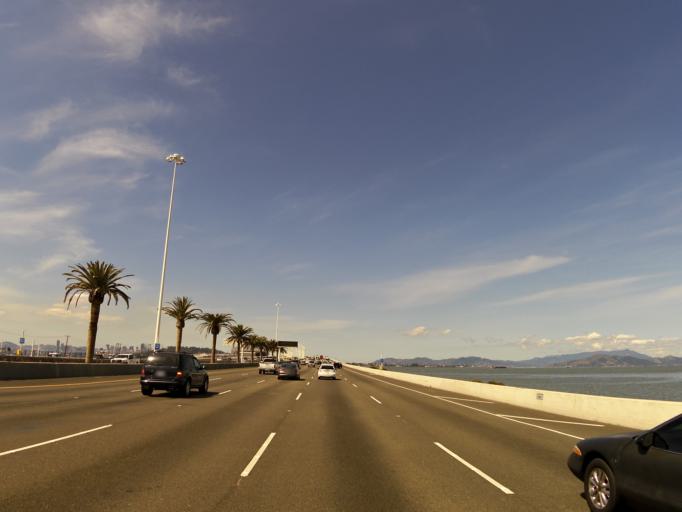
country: US
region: California
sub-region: Alameda County
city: Emeryville
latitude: 37.8225
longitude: -122.3244
